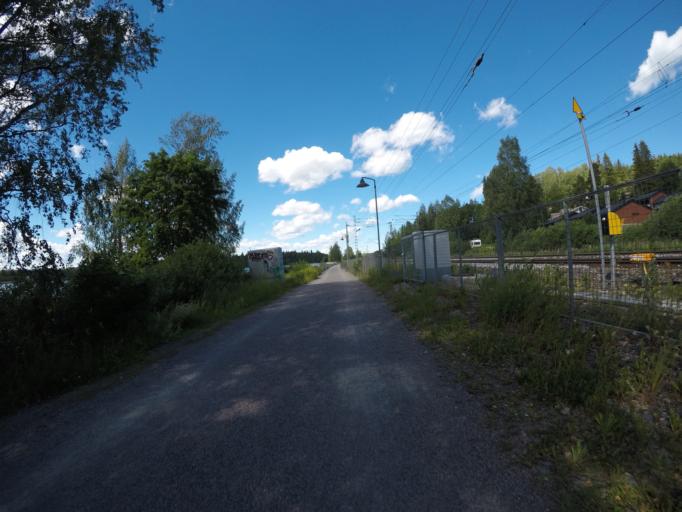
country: FI
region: Haeme
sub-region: Haemeenlinna
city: Haemeenlinna
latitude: 61.0060
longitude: 24.4689
